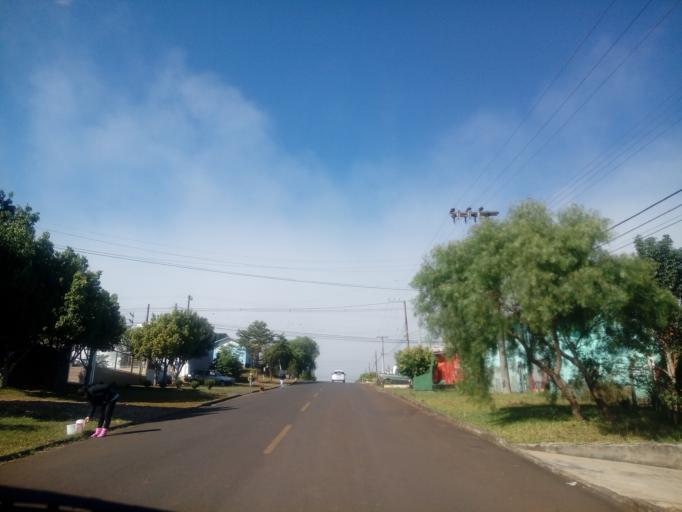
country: BR
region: Santa Catarina
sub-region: Chapeco
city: Chapeco
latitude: -27.0812
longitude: -52.6099
